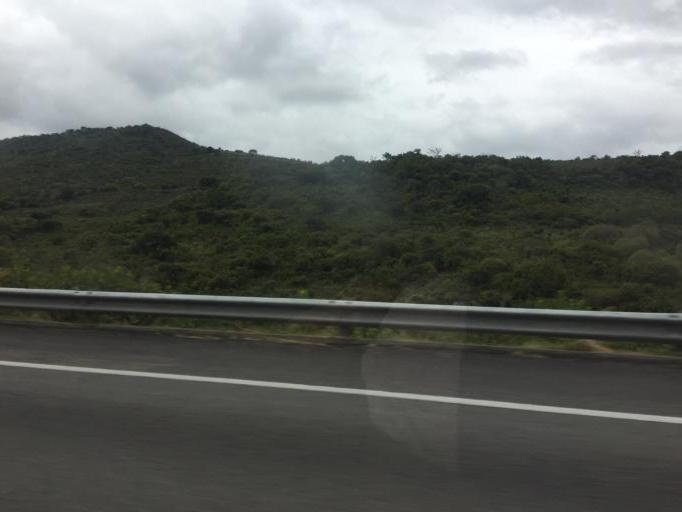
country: MX
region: Jalisco
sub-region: Zapotlan del Rey
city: Zapotlan del Rey
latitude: 20.5180
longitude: -102.9825
